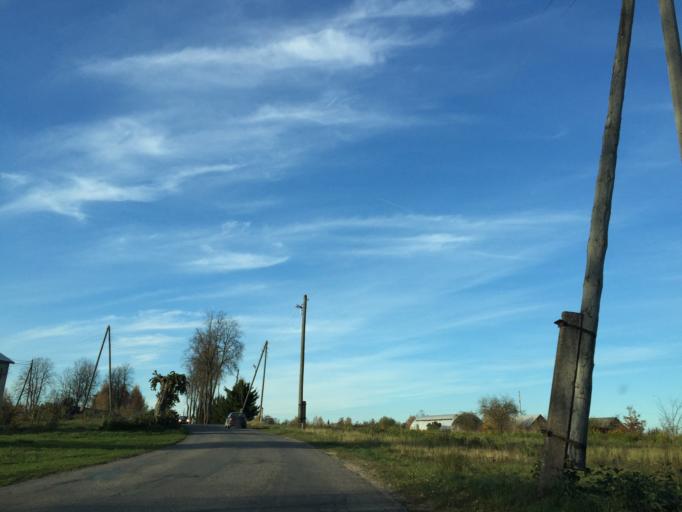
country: LV
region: Skriveri
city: Skriveri
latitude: 56.6289
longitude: 25.1229
